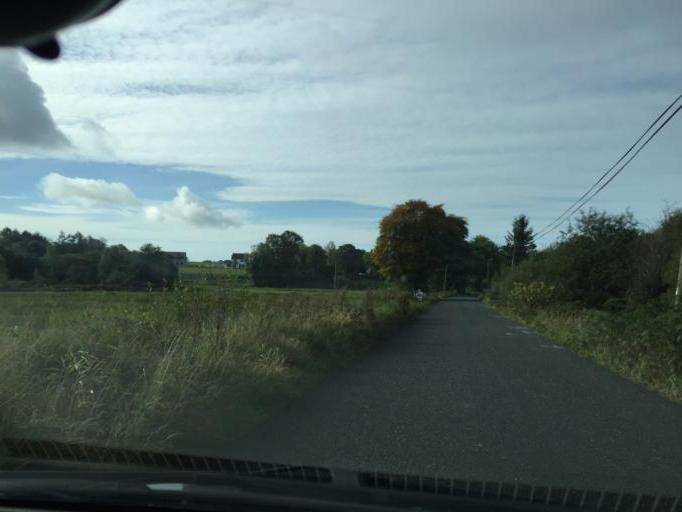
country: IE
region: Connaught
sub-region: Roscommon
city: Boyle
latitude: 54.0606
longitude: -8.2332
